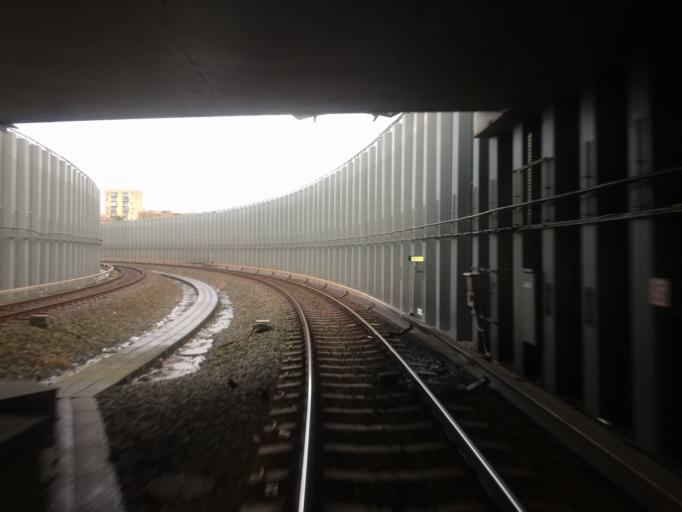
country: DK
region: Capital Region
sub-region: Kobenhavn
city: Christianshavn
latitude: 55.6618
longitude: 12.6289
